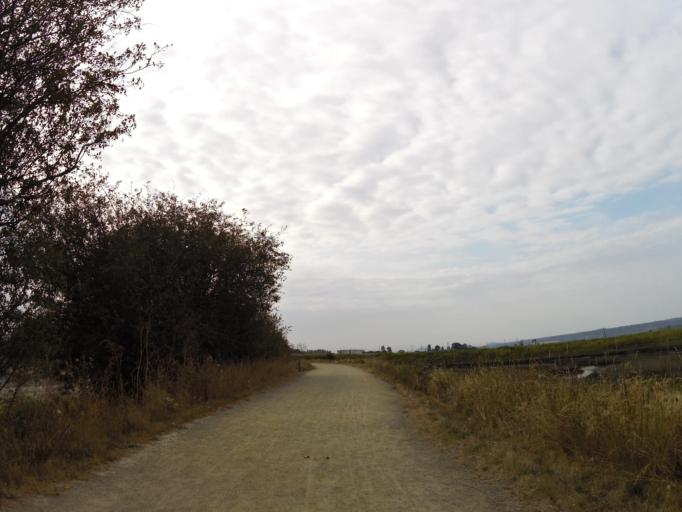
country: US
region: Washington
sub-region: Skagit County
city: Mount Vernon
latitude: 48.4574
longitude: -122.4686
